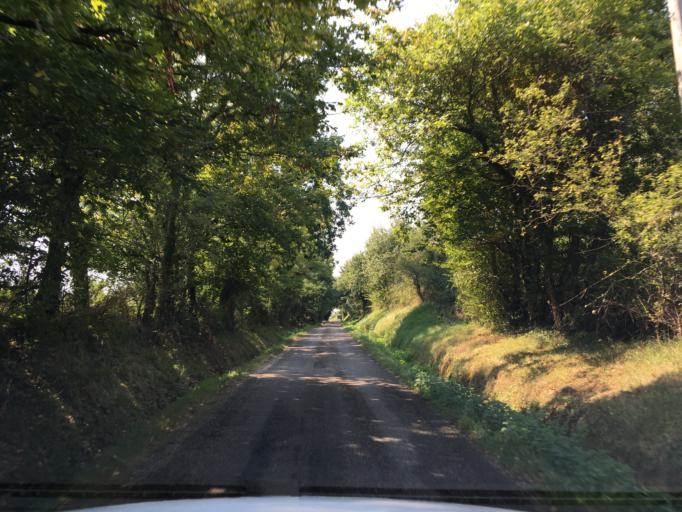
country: FR
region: Midi-Pyrenees
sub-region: Departement du Tarn-et-Garonne
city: Saint-Nauphary
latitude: 44.0058
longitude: 1.4150
